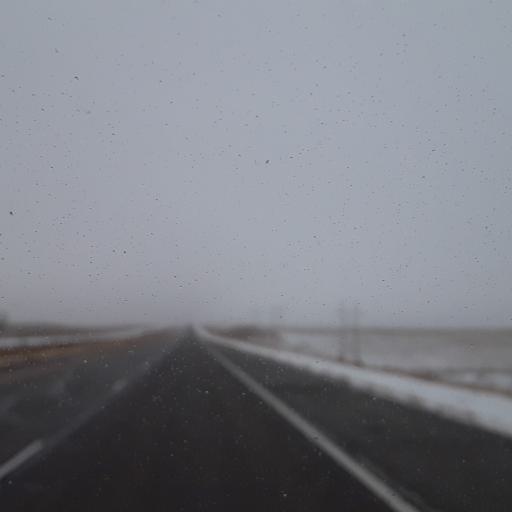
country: US
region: Nebraska
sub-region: Cheyenne County
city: Sidney
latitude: 40.8036
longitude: -102.8597
